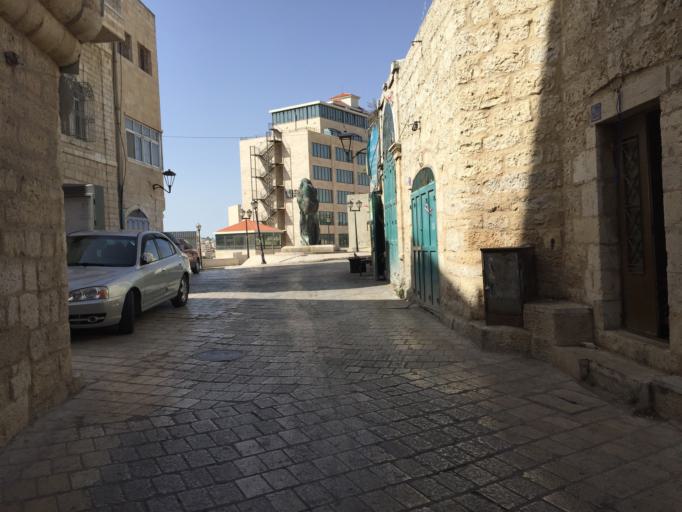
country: PS
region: West Bank
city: Bethlehem
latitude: 31.7088
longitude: 35.2043
